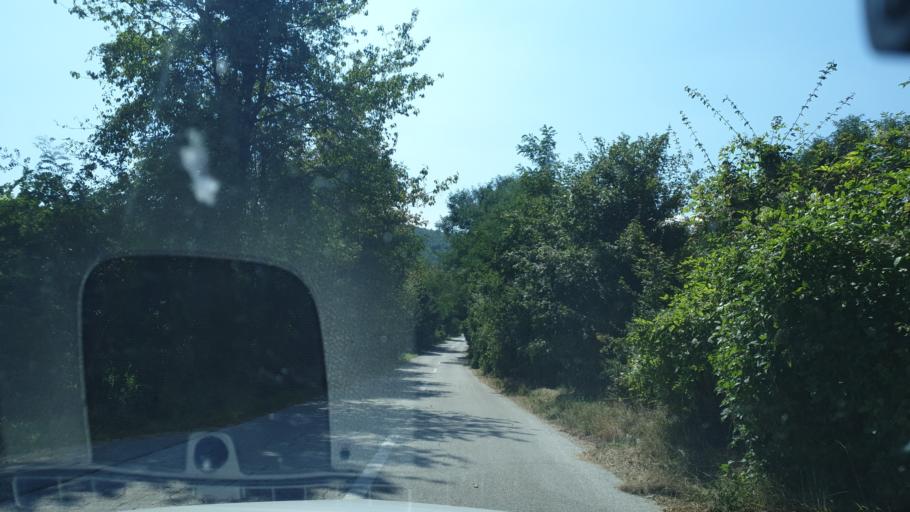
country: RS
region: Central Serbia
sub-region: Zlatiborski Okrug
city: Cajetina
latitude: 43.6842
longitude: 19.8475
